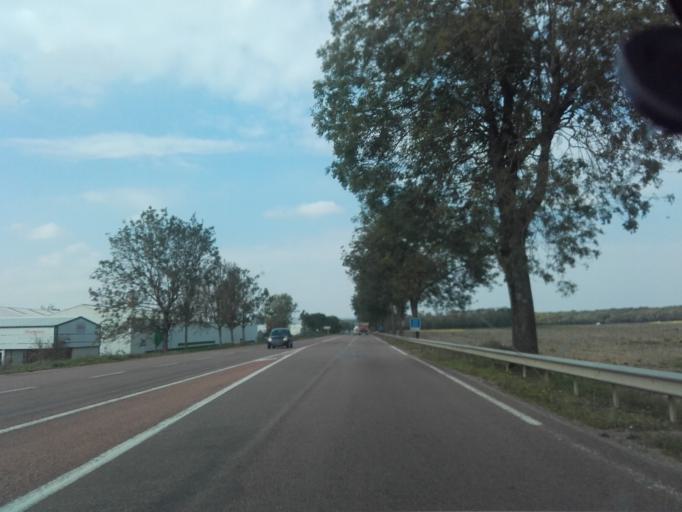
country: FR
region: Bourgogne
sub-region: Departement de Saone-et-Loire
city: Fontaines
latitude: 46.8595
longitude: 4.7994
